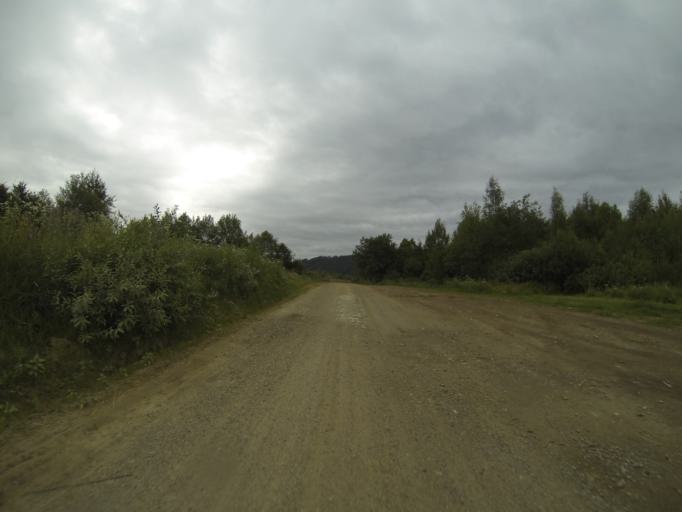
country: RO
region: Brasov
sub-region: Comuna Sinca Noua
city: Sinca Noua
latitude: 45.7292
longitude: 25.2235
